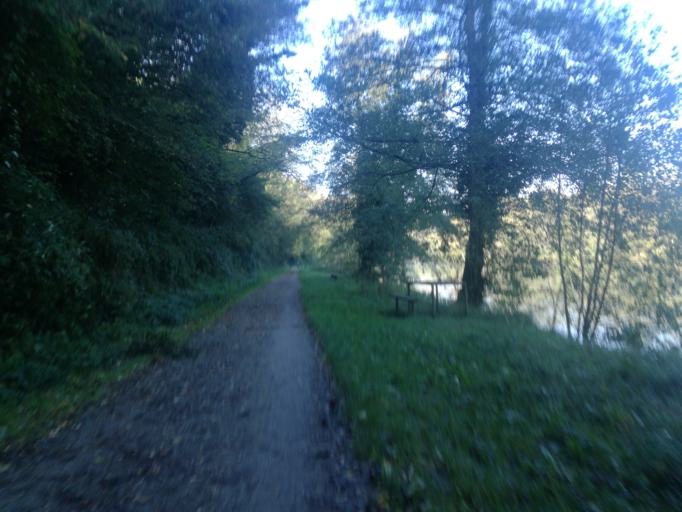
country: IT
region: Lombardy
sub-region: Provincia di Bergamo
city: Bottanuco
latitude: 45.6293
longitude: 9.4993
